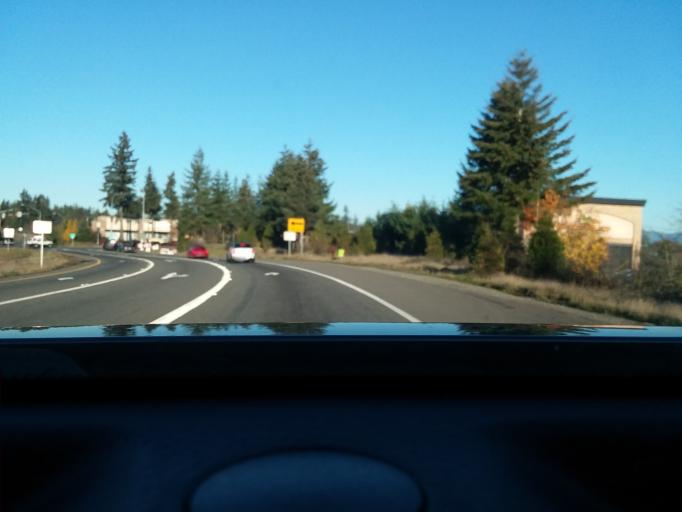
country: US
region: Washington
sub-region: King County
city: Covington
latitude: 47.3571
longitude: -122.1209
